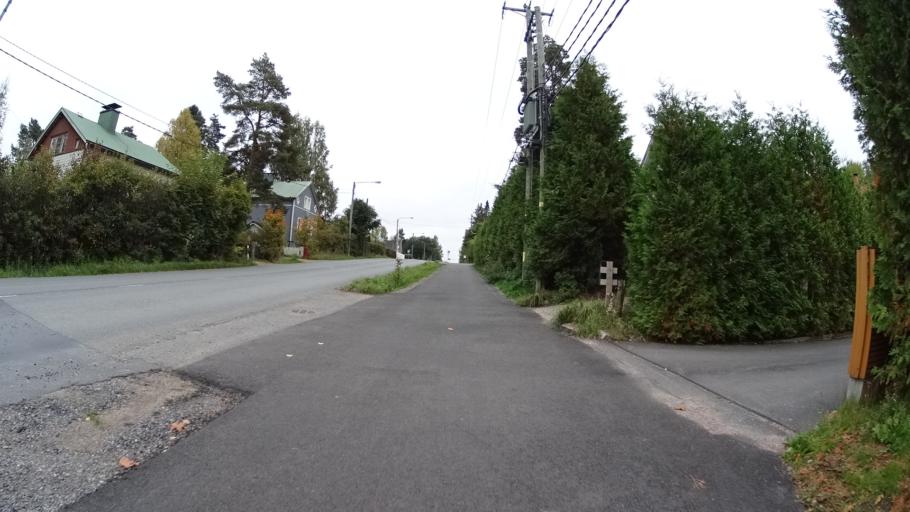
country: FI
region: Uusimaa
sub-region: Helsinki
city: Kilo
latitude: 60.2404
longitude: 24.8086
